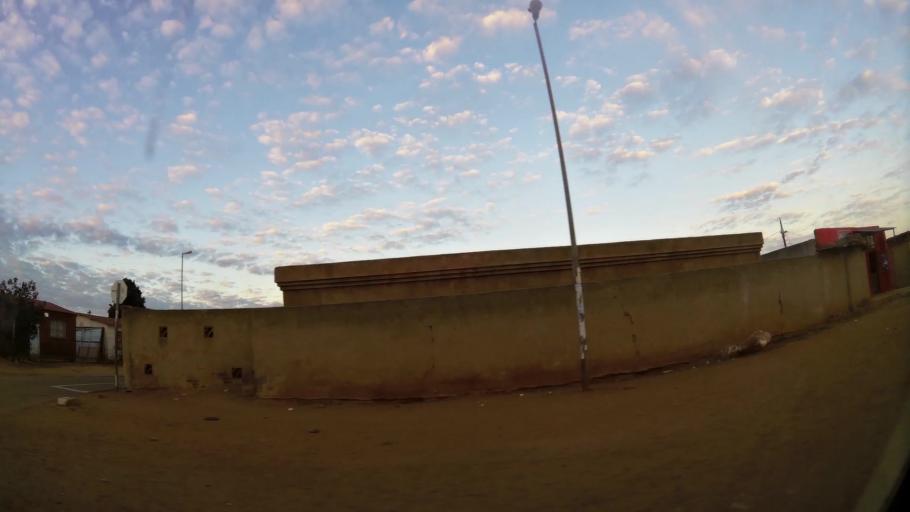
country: ZA
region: Gauteng
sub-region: City of Tshwane Metropolitan Municipality
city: Pretoria
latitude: -25.7070
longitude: 28.3323
